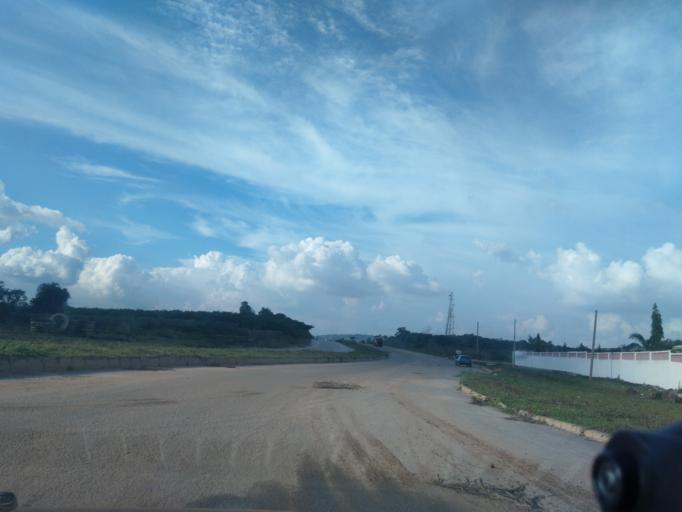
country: NG
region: Abuja Federal Capital Territory
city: Abuja
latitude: 9.0396
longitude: 7.3875
